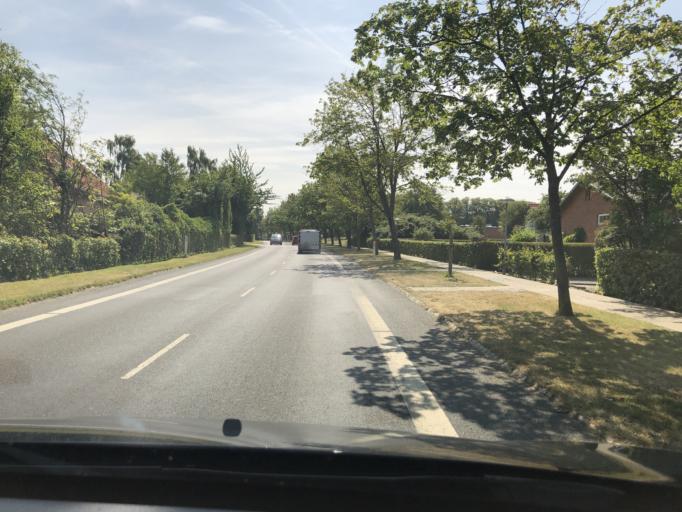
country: DK
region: South Denmark
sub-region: AEro Kommune
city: AEroskobing
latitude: 54.8907
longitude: 10.4084
